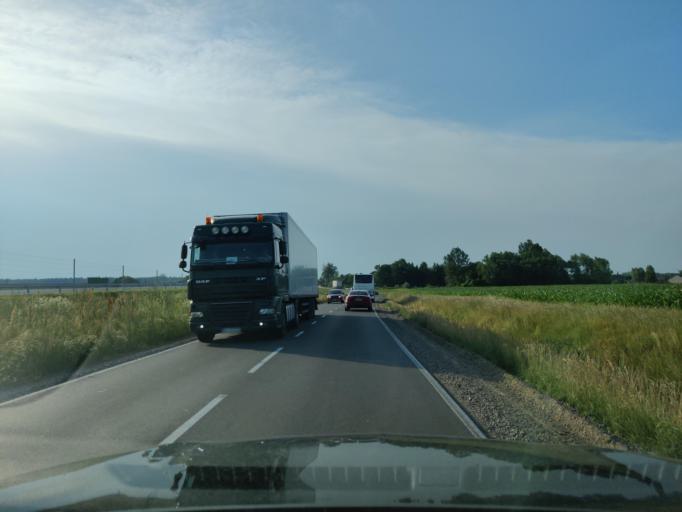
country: PL
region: Masovian Voivodeship
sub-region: Powiat plonski
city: Plonsk
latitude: 52.6869
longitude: 20.3589
